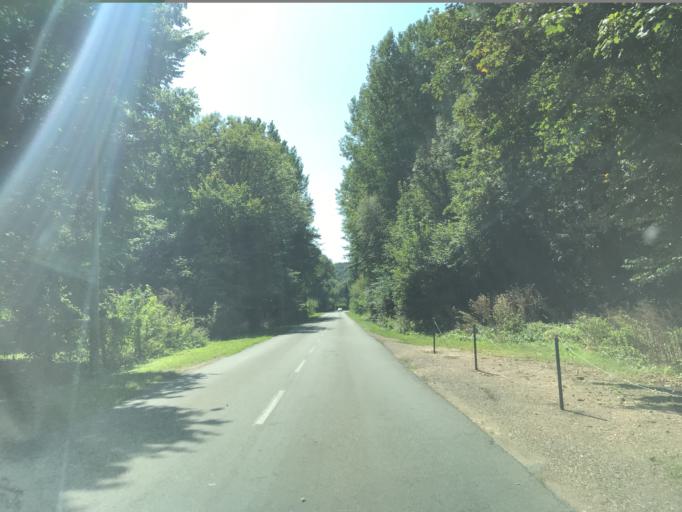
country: FR
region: Haute-Normandie
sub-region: Departement de l'Eure
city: Houlbec-Cocherel
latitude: 49.0707
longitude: 1.2960
